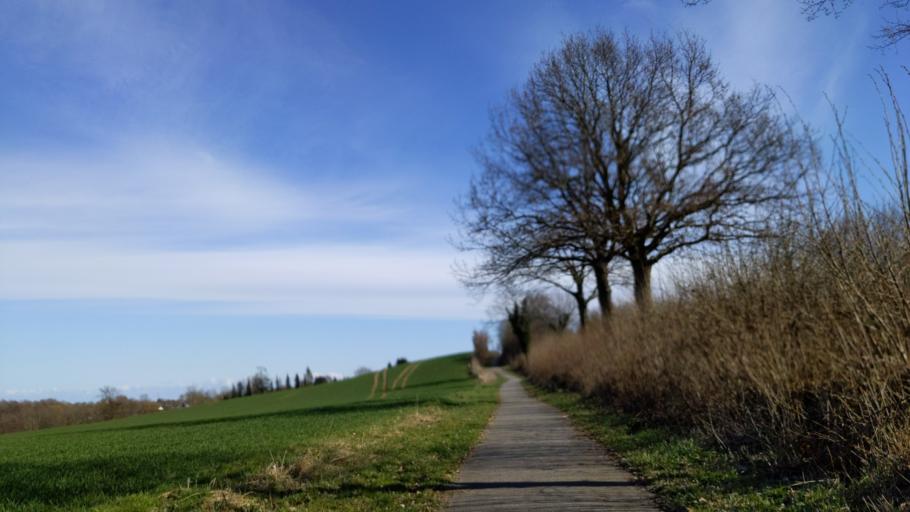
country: DE
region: Schleswig-Holstein
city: Susel
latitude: 54.1089
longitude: 10.7001
